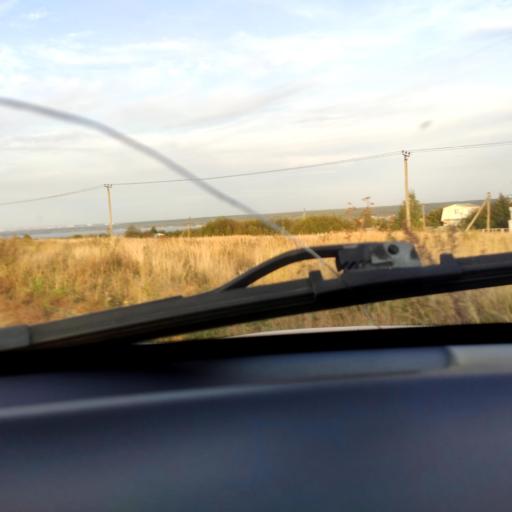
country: RU
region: Tatarstan
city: Verkhniy Uslon
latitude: 55.6509
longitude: 48.9438
